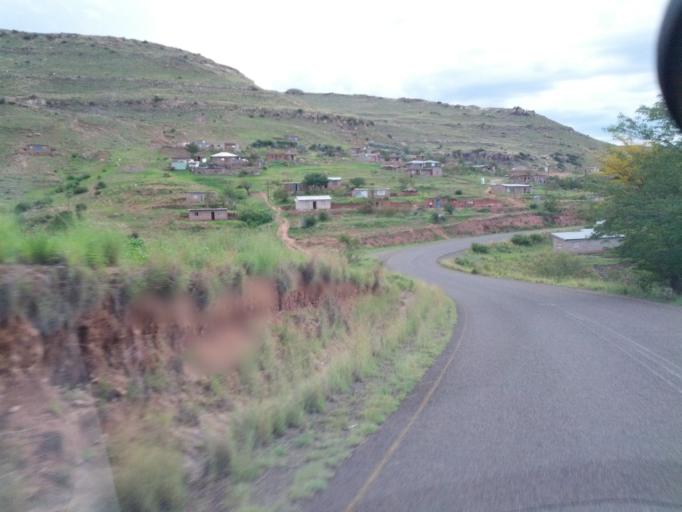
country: LS
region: Qacha's Nek
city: Qacha's Nek
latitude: -30.0664
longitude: 28.5444
